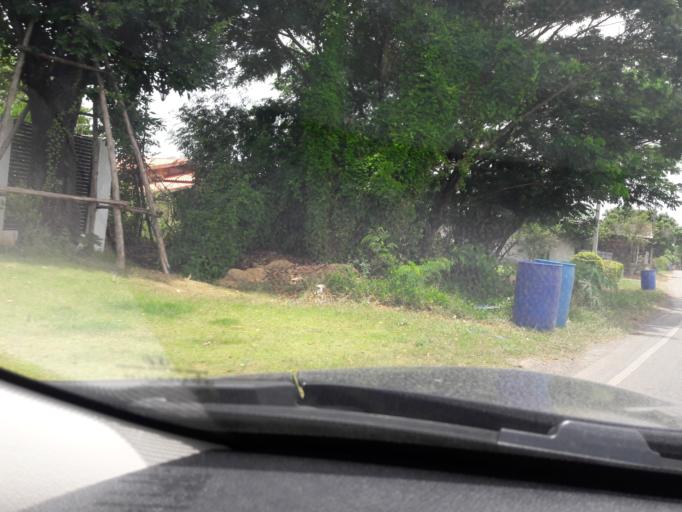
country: TH
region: Ratchaburi
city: Damnoen Saduak
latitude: 13.5920
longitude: 99.9493
